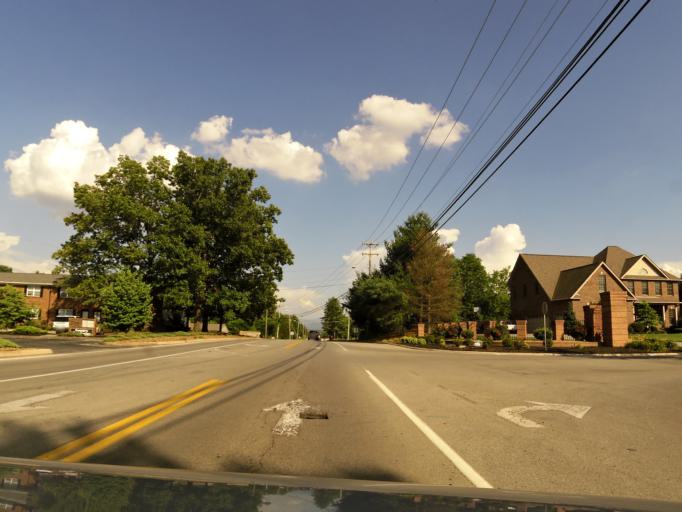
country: US
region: Tennessee
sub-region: Blount County
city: Alcoa
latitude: 35.7828
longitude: -84.0028
